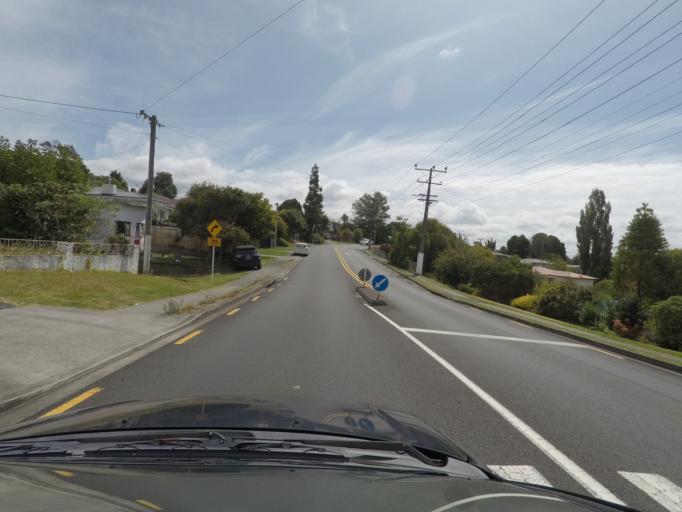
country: NZ
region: Auckland
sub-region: Auckland
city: Waitakere
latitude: -36.9032
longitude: 174.6682
